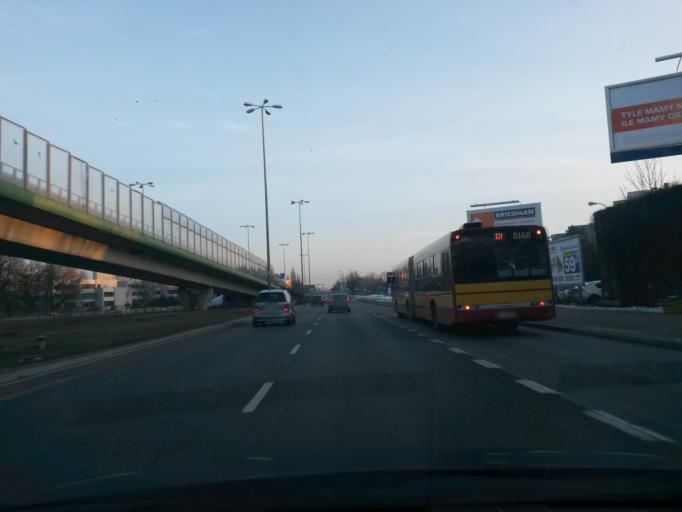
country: PL
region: Masovian Voivodeship
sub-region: Warszawa
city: Mokotow
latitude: 52.1966
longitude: 21.0522
